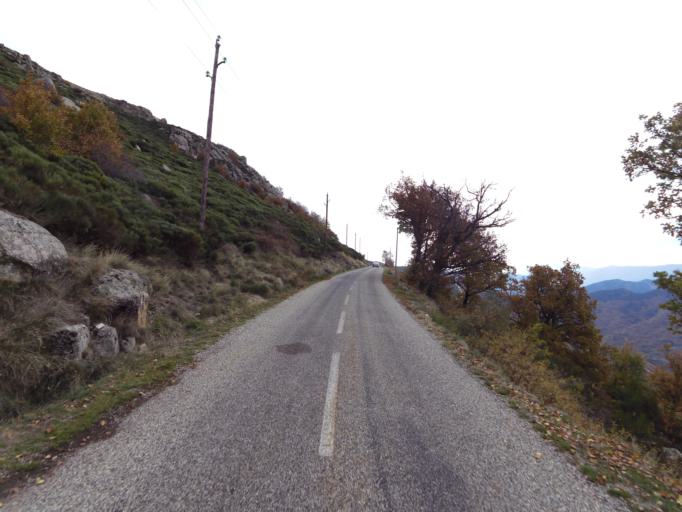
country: FR
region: Rhone-Alpes
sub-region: Departement de l'Ardeche
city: Les Vans
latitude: 44.5125
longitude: 4.0368
